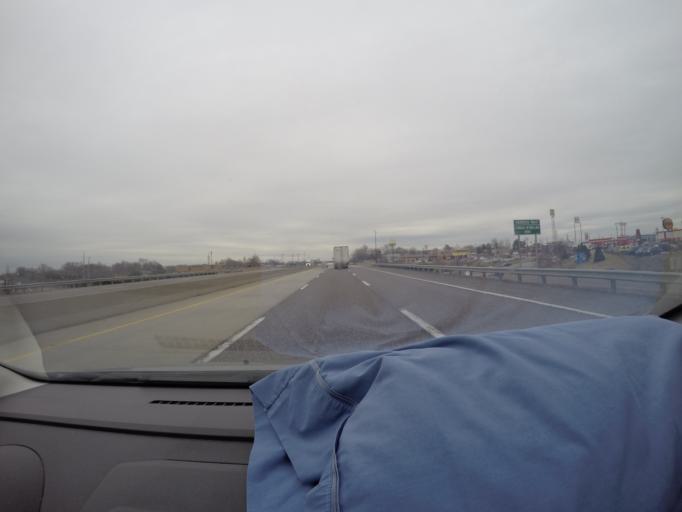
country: US
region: Missouri
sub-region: Saint Charles County
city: O'Fallon
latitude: 38.8024
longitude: -90.7014
